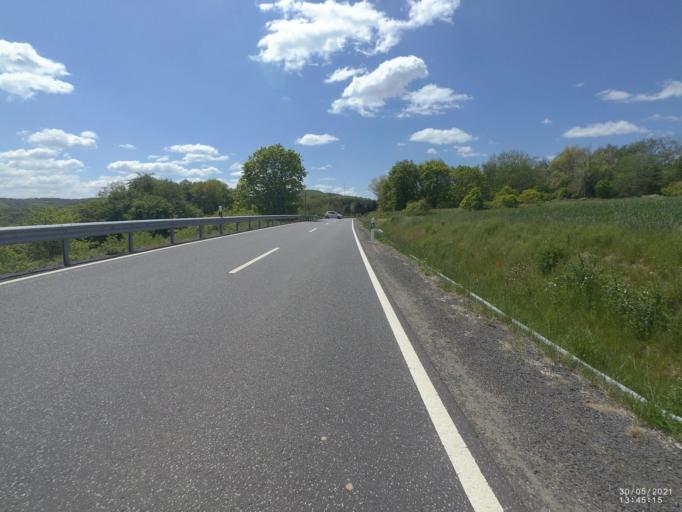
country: DE
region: Rheinland-Pfalz
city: Waldesch
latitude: 50.2781
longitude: 7.5610
